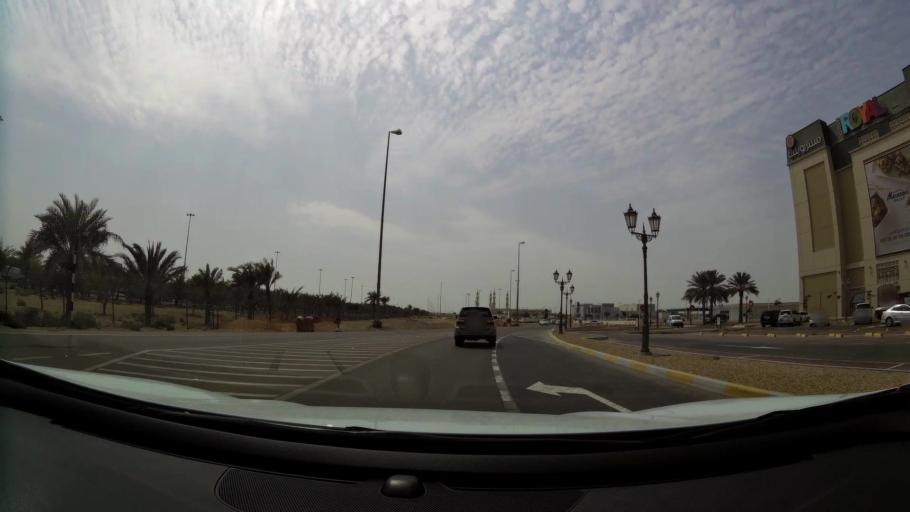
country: AE
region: Abu Dhabi
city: Abu Dhabi
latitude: 24.5220
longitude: 54.6710
